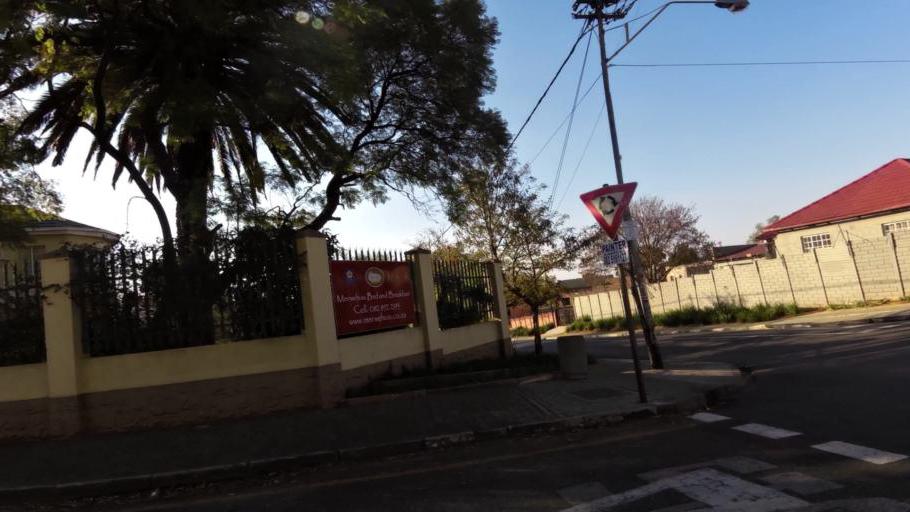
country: ZA
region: Gauteng
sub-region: City of Johannesburg Metropolitan Municipality
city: Johannesburg
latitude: -26.1900
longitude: 27.9968
